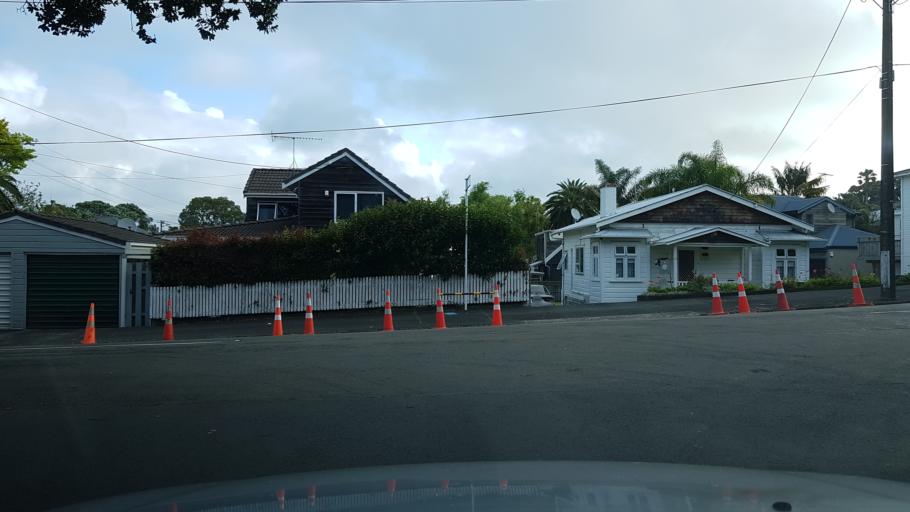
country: NZ
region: Auckland
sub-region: Auckland
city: North Shore
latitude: -36.8160
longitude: 174.7484
